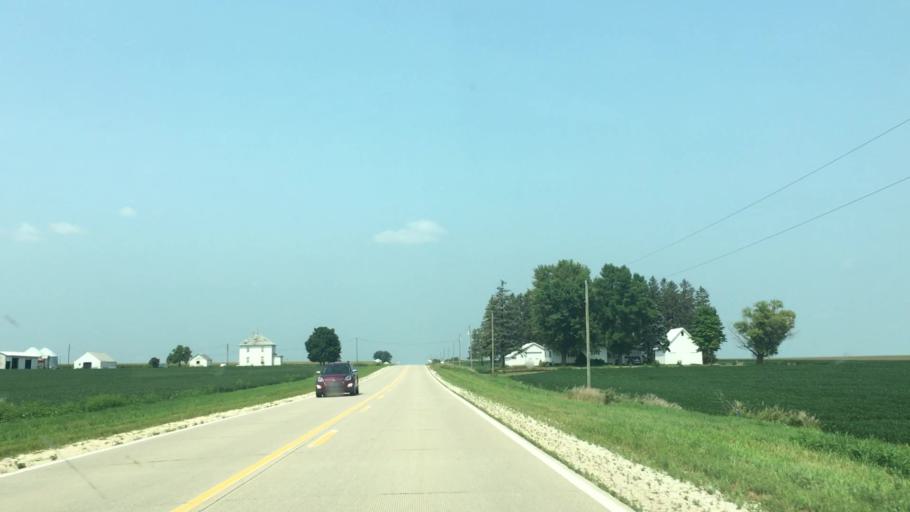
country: US
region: Iowa
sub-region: Fayette County
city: Oelwein
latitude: 42.7090
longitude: -91.8048
